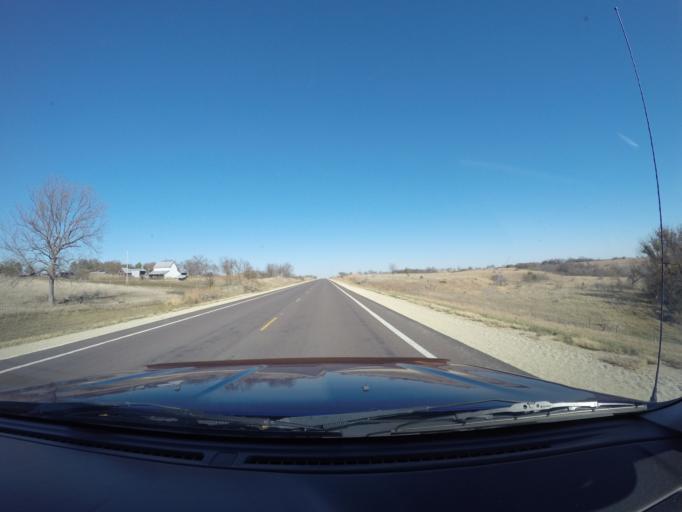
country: US
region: Kansas
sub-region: Marshall County
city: Blue Rapids
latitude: 39.6643
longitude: -96.7505
